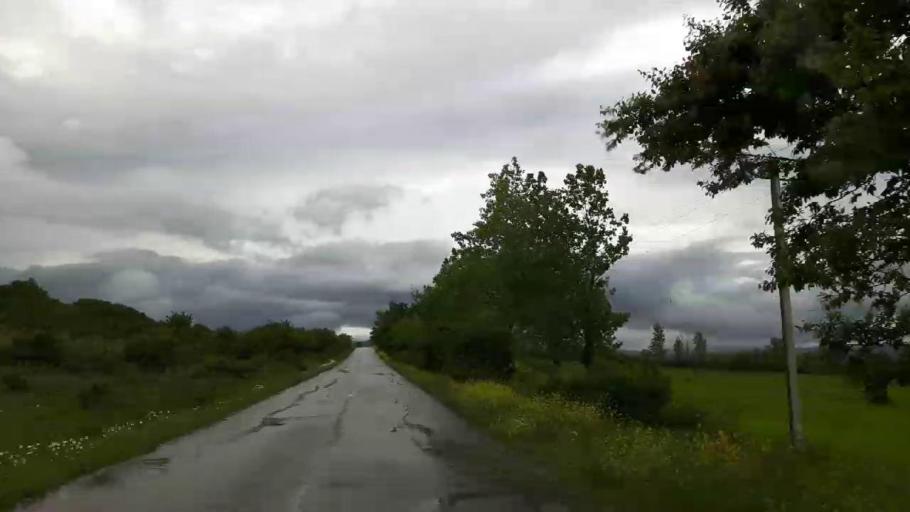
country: GE
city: Agara
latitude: 41.9926
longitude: 43.7198
